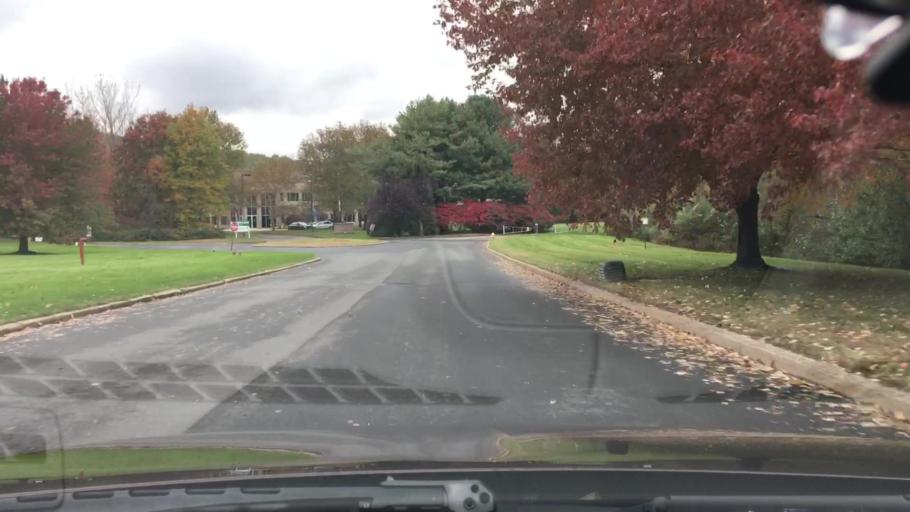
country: US
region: Connecticut
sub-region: New Haven County
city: Cheshire Village
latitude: 41.5528
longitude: -72.9192
